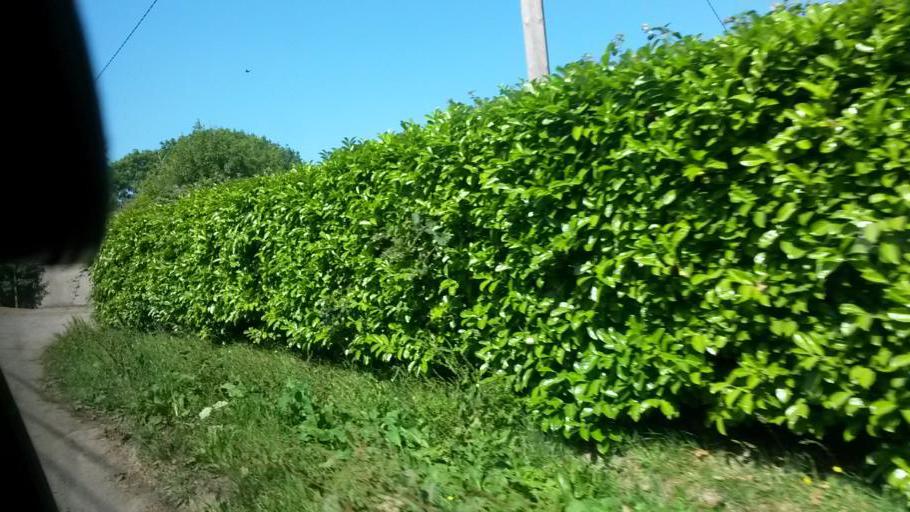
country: IE
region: Leinster
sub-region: Fingal County
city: Swords
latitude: 53.4854
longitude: -6.2851
